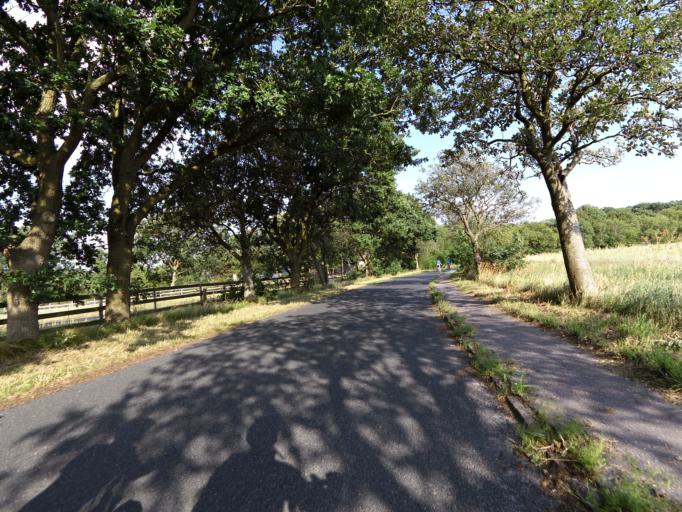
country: DE
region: Lower Saxony
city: Nordholz
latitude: 53.8274
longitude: 8.5834
